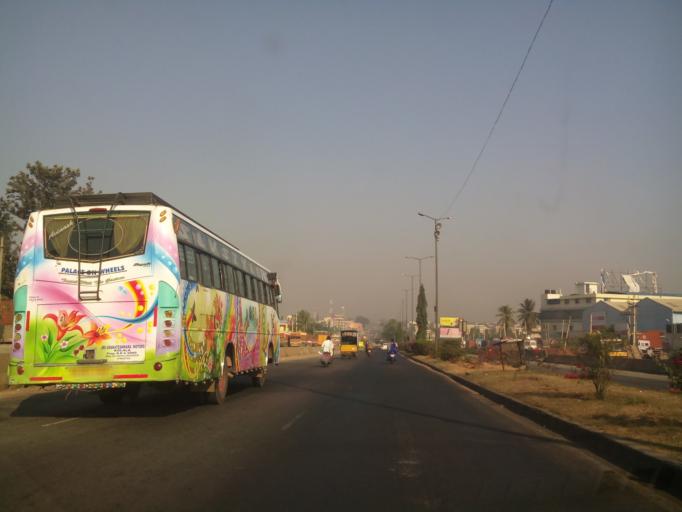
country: IN
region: Karnataka
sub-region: Bangalore Rural
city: Nelamangala
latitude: 13.0613
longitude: 77.4608
